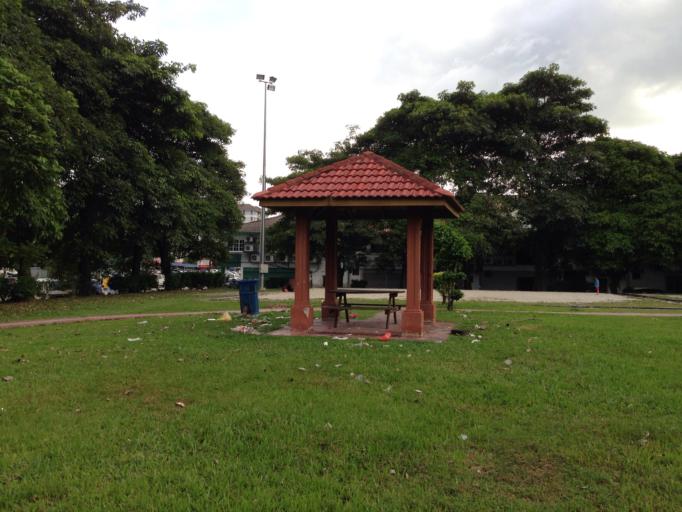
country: MY
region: Kuala Lumpur
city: Kuala Lumpur
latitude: 3.1324
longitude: 101.7553
